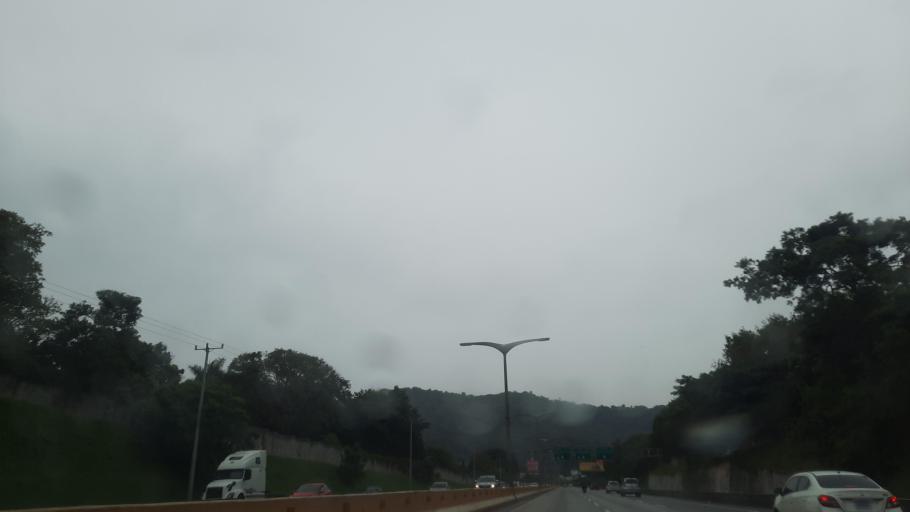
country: SV
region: La Libertad
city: Santa Tecla
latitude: 13.6836
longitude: -89.2977
